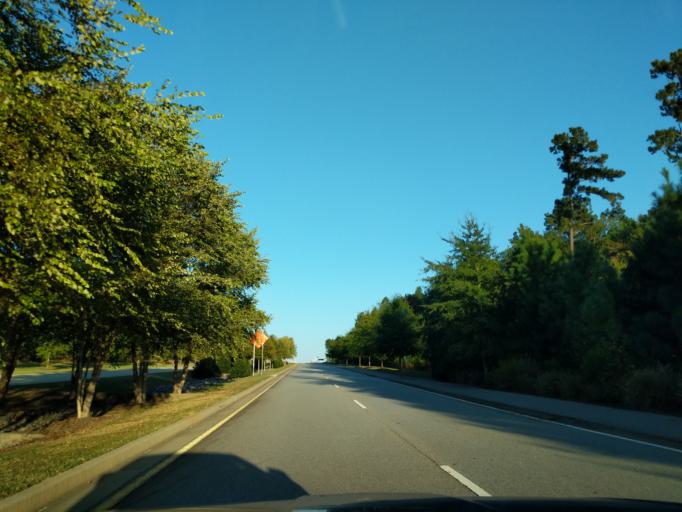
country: US
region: Georgia
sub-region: Columbia County
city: Grovetown
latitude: 33.4794
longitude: -82.1888
